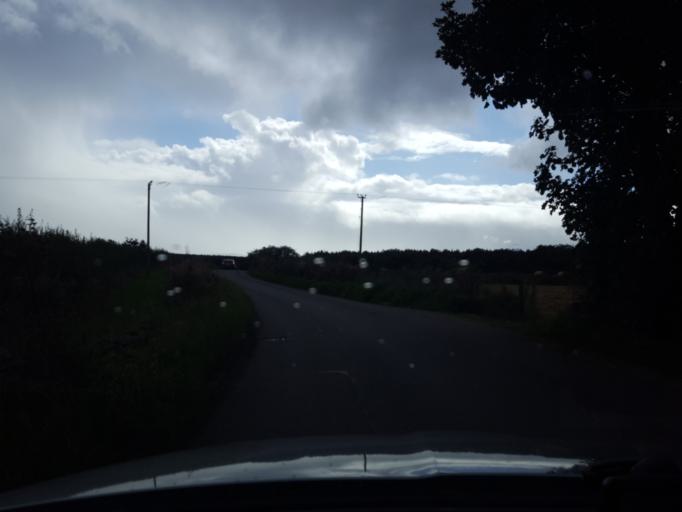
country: GB
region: Scotland
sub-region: Aberdeenshire
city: Banchory
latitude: 57.0897
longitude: -2.4479
